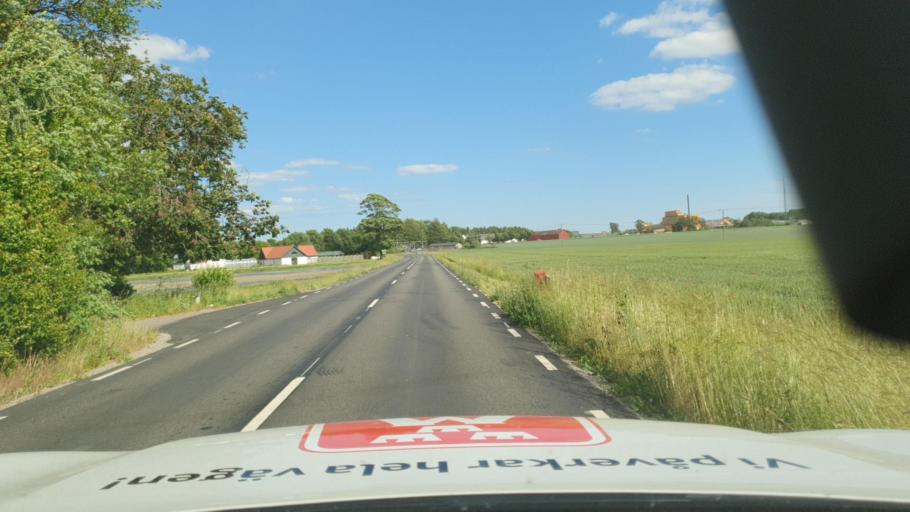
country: SE
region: Skane
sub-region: Ystads Kommun
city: Kopingebro
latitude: 55.4680
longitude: 13.9251
